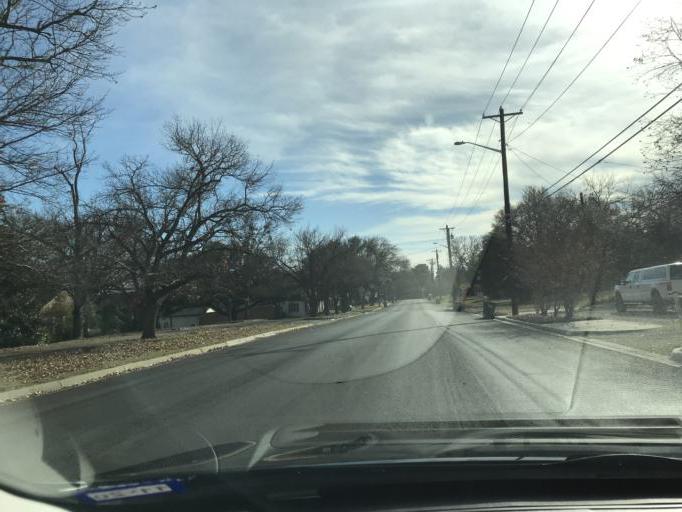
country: US
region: Texas
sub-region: Denton County
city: Denton
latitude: 33.2209
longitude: -97.1551
